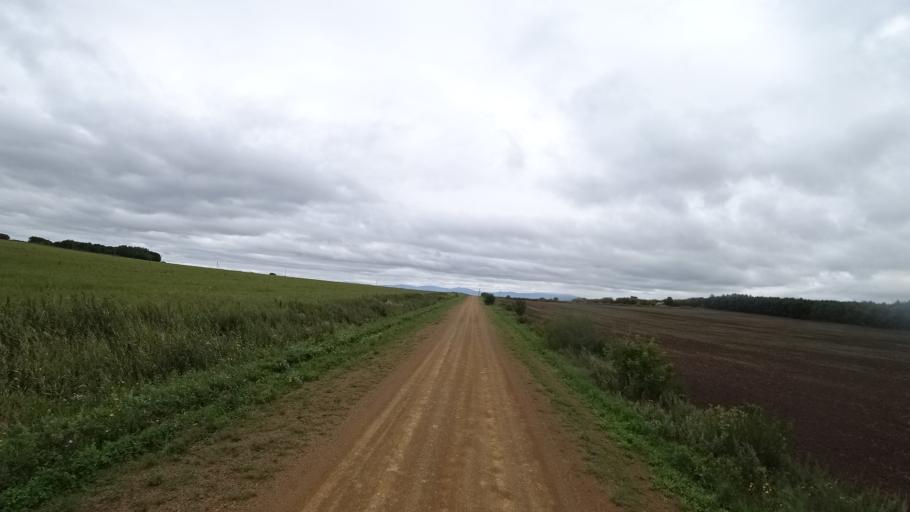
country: RU
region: Primorskiy
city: Chernigovka
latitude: 44.4358
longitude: 132.5880
